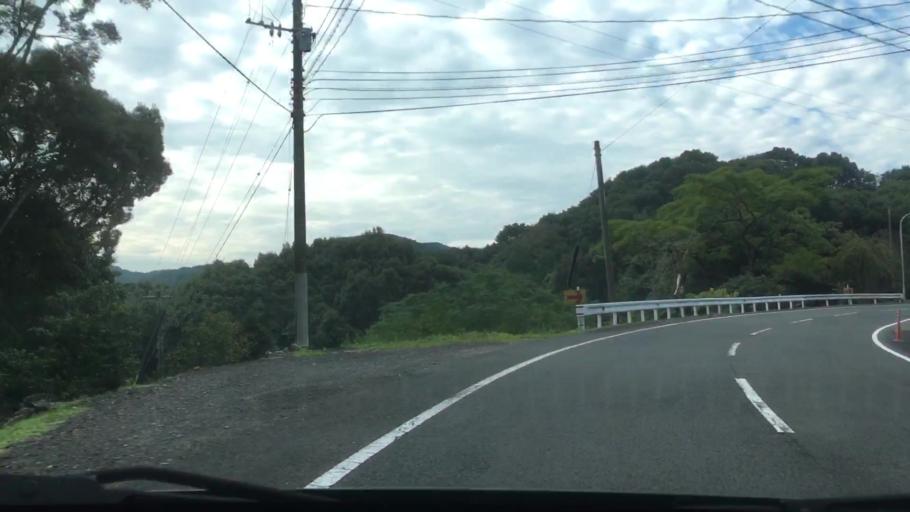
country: JP
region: Nagasaki
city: Sasebo
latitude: 32.9827
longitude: 129.7179
